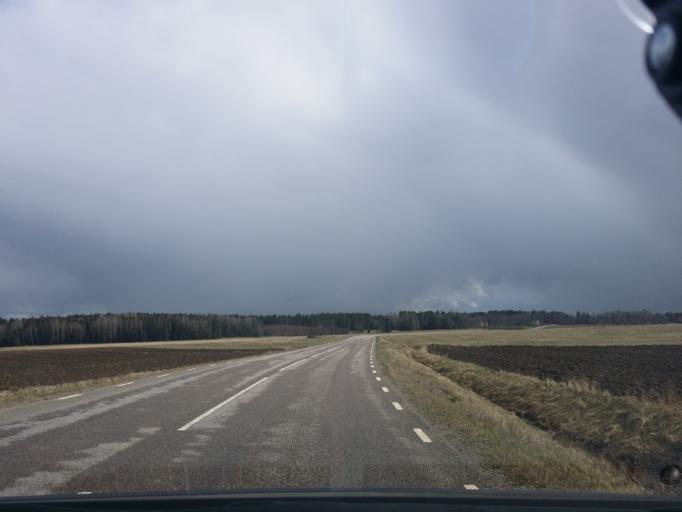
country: SE
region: Vaestmanland
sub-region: Sala Kommun
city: Sala
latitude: 59.9111
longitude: 16.6424
